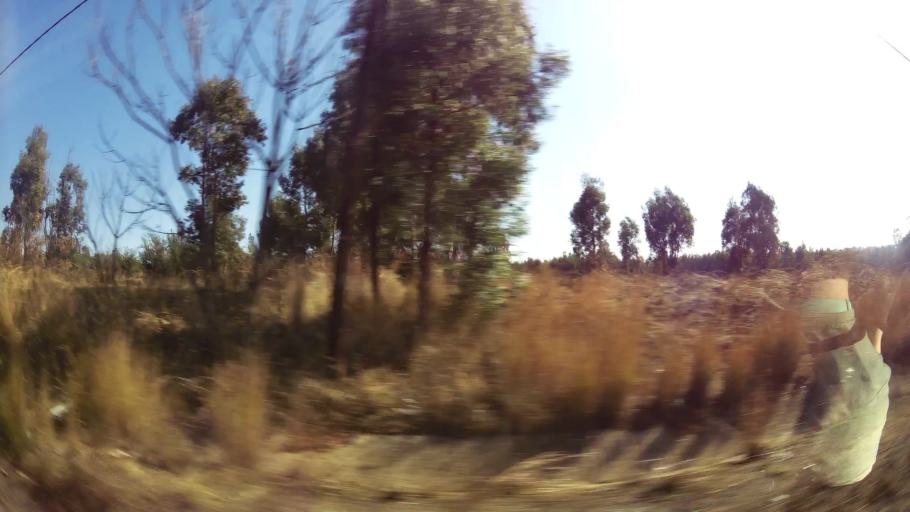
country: ZA
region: Mpumalanga
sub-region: Nkangala District Municipality
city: Witbank
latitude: -25.8397
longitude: 29.2448
